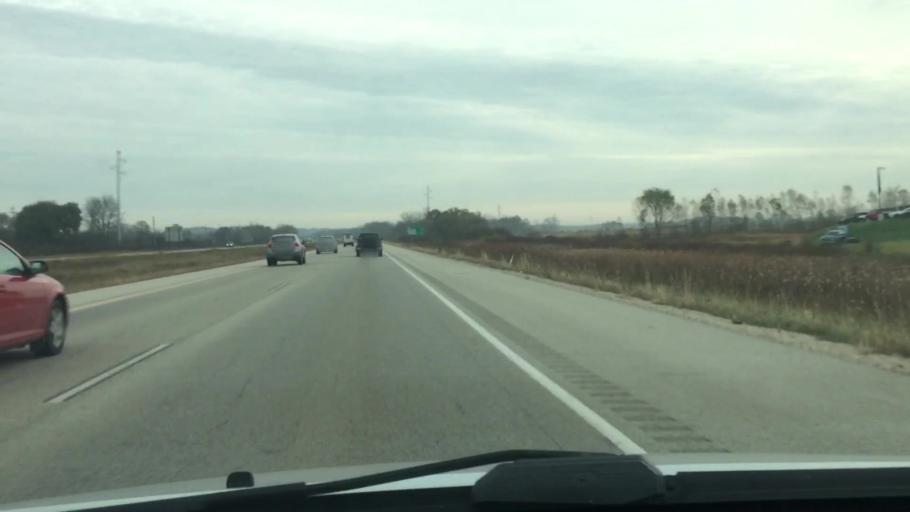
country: US
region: Wisconsin
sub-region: Waukesha County
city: Mukwonago
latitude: 42.8592
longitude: -88.3095
